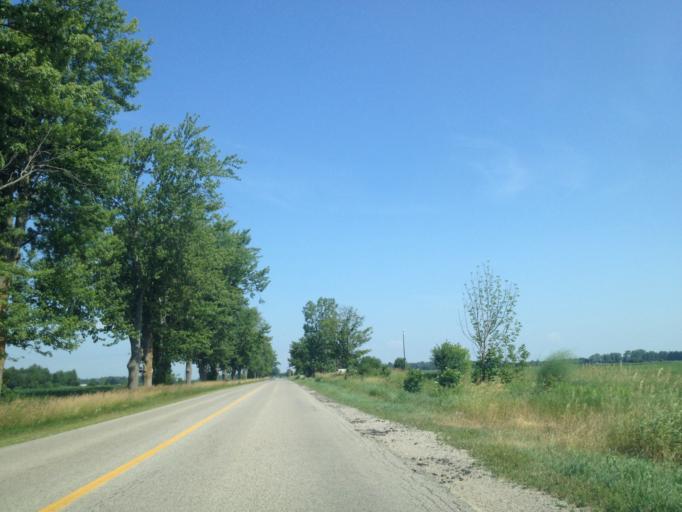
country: CA
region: Ontario
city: London
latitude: 43.0883
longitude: -81.2172
